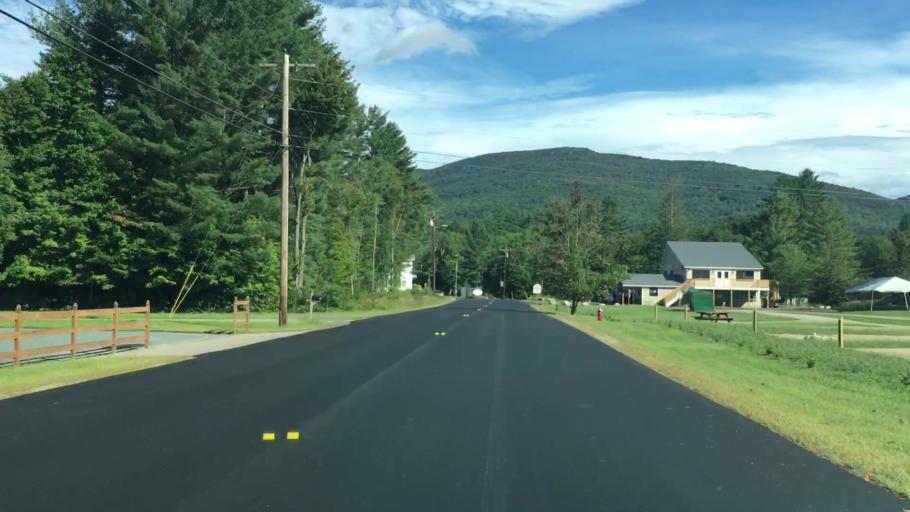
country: US
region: New Hampshire
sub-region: Grafton County
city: Woodstock
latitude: 44.0319
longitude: -71.6950
